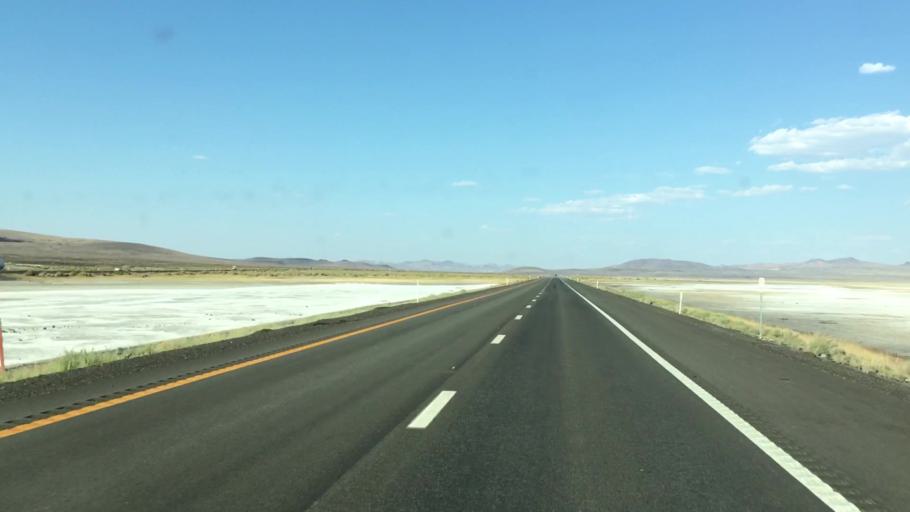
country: US
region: Nevada
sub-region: Lyon County
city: Fernley
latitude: 39.7059
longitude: -119.0946
